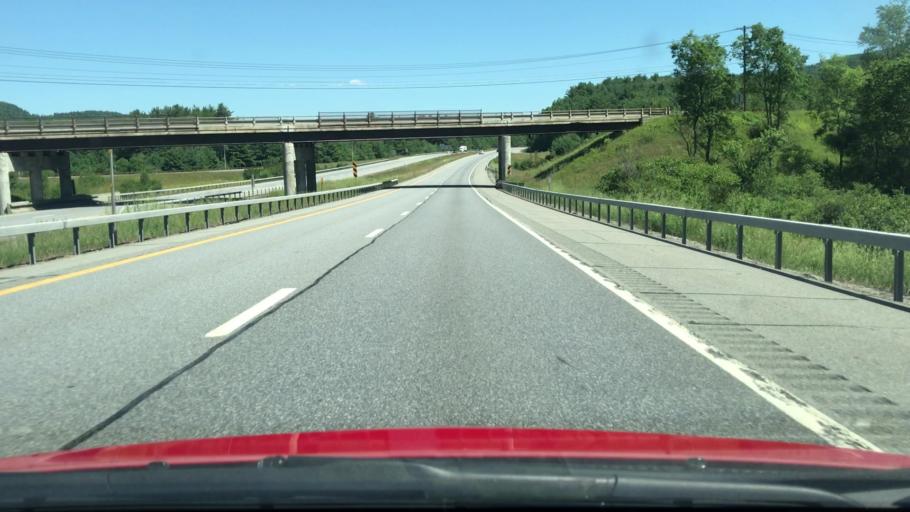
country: US
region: New York
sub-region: Warren County
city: Warrensburg
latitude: 43.4864
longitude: -73.7534
